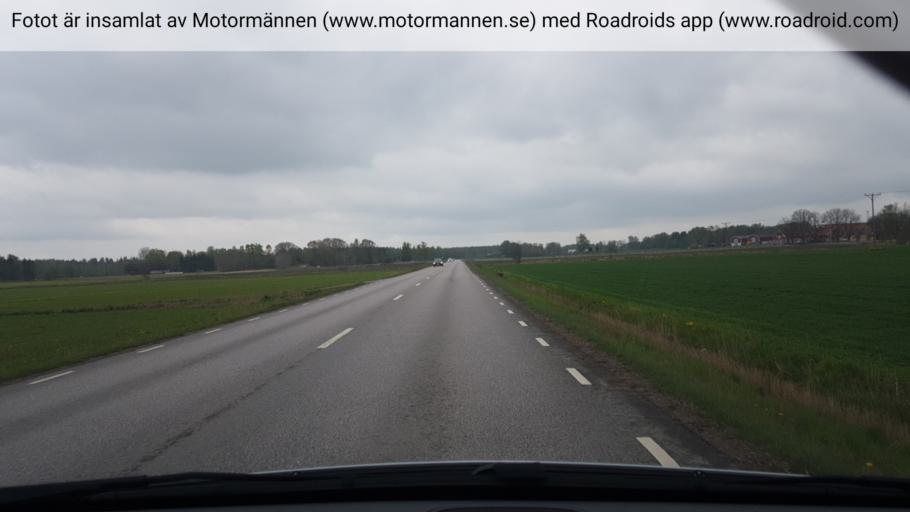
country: SE
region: Vaestra Goetaland
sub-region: Skovde Kommun
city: Stopen
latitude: 58.5360
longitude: 13.9975
